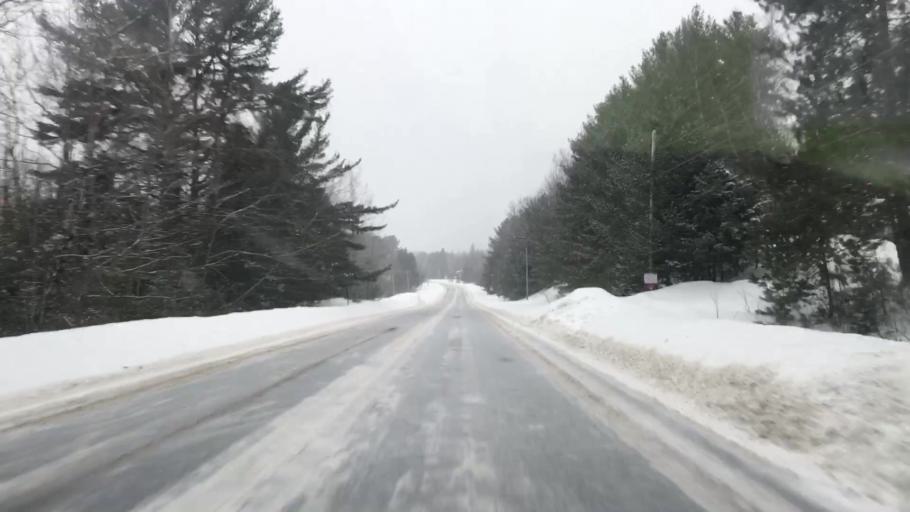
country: US
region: Maine
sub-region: Penobscot County
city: Medway
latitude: 45.5399
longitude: -68.3680
